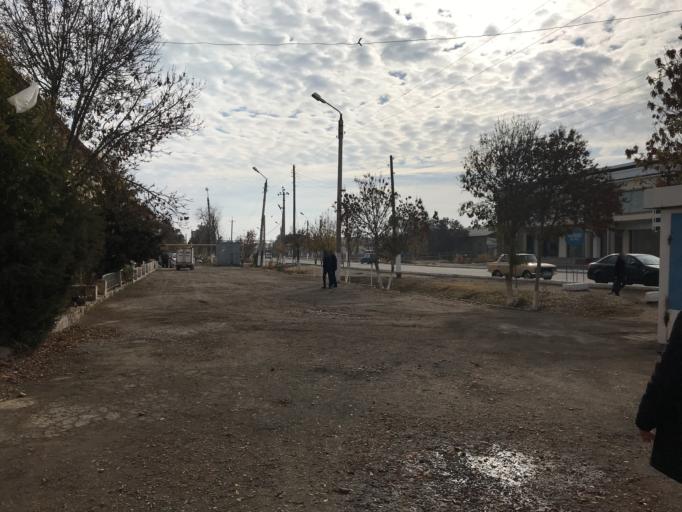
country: UZ
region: Bukhara
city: Kogon
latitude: 39.7212
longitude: 64.5522
